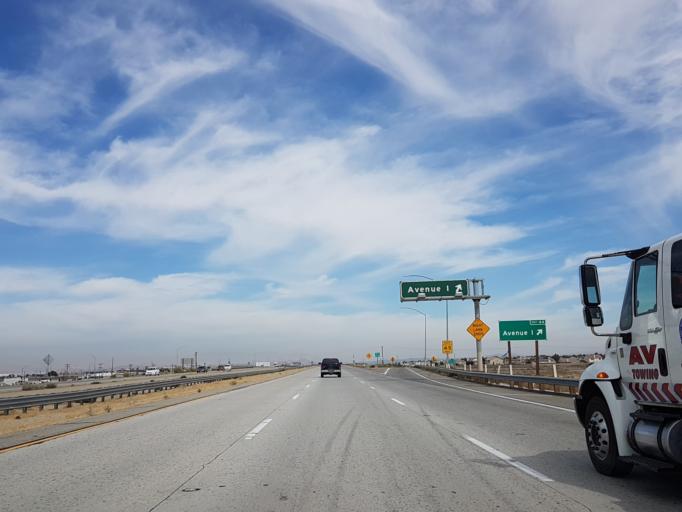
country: US
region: California
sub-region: Los Angeles County
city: Lancaster
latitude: 34.7004
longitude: -118.1699
